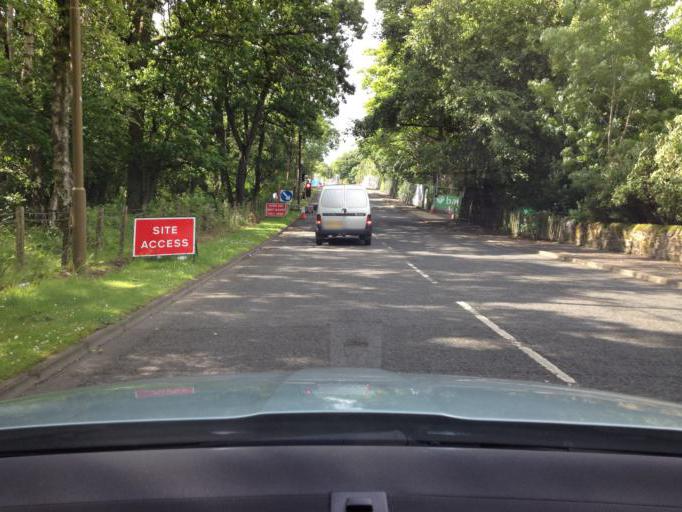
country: GB
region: Scotland
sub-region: West Lothian
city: Livingston
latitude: 55.8633
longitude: -3.5198
